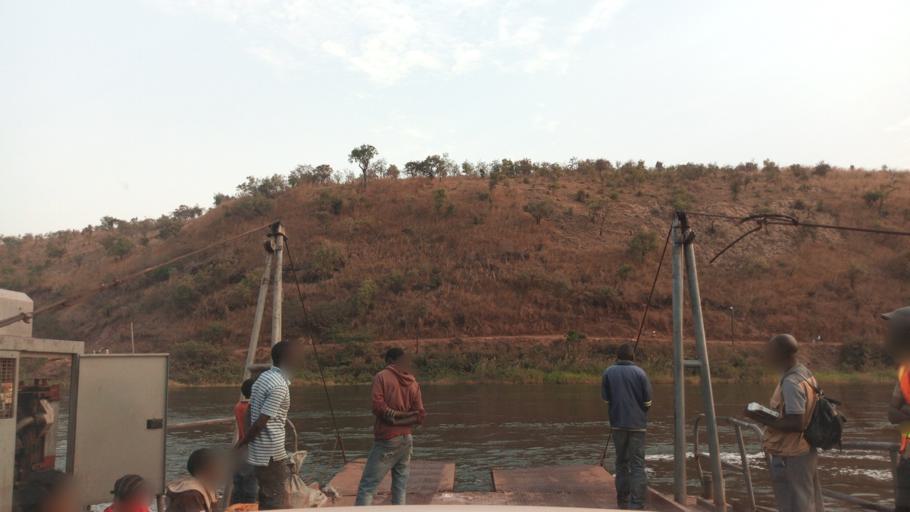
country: ZM
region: Northern
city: Kaputa
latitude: -8.4818
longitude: 28.8843
